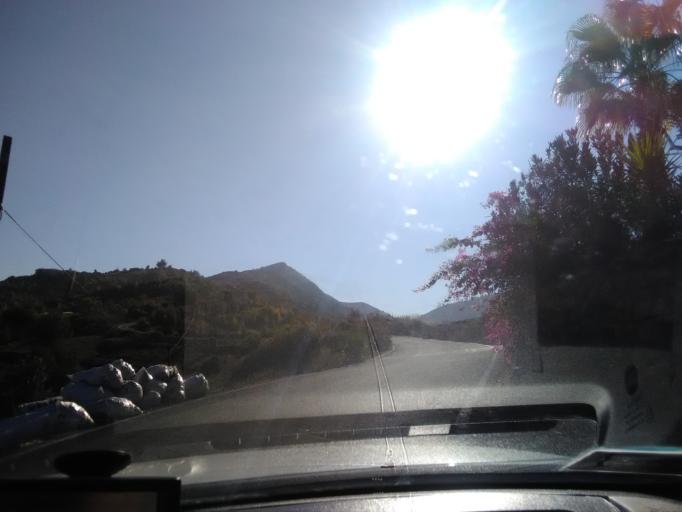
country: TR
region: Antalya
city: Gazipasa
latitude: 36.2534
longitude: 32.3305
